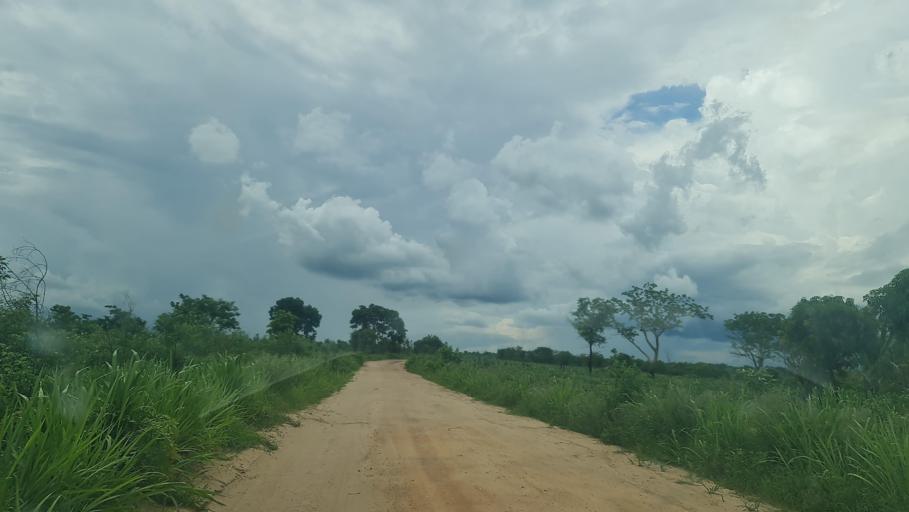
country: MW
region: Southern Region
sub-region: Nsanje District
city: Nsanje
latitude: -17.5766
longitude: 35.6577
